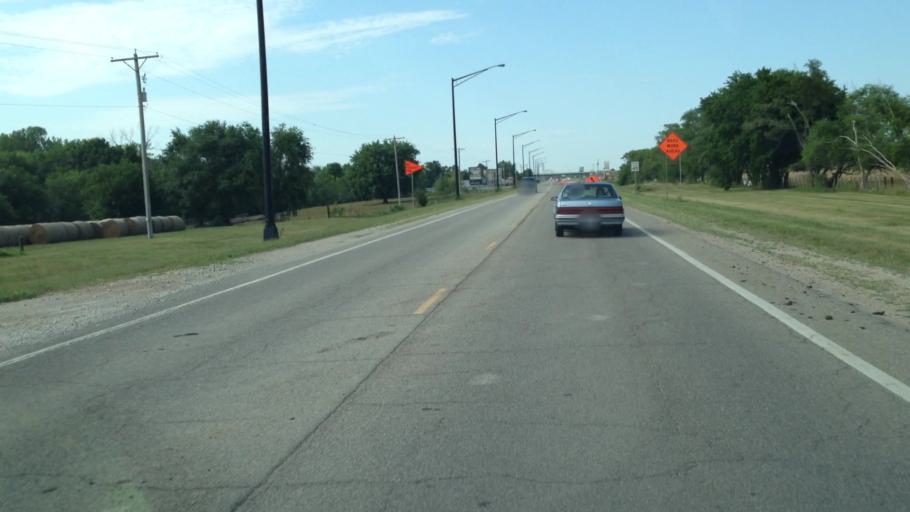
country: US
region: Kansas
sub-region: Labette County
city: Parsons
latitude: 37.3582
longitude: -95.2586
